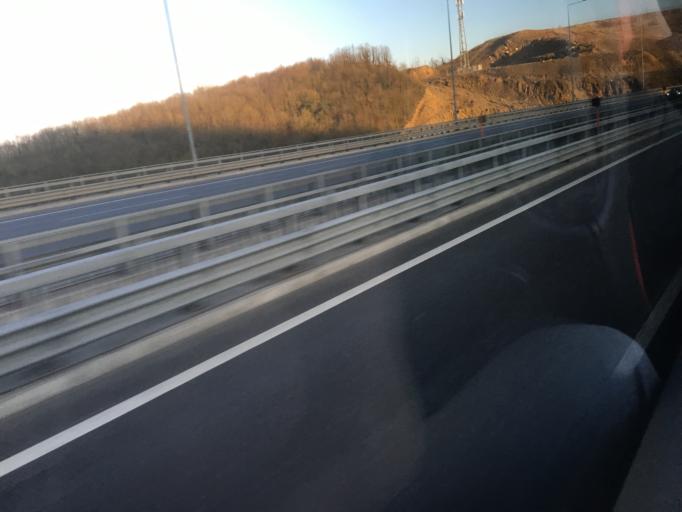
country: TR
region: Istanbul
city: Mahmut Sevket Pasa
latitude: 41.1386
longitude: 29.2858
